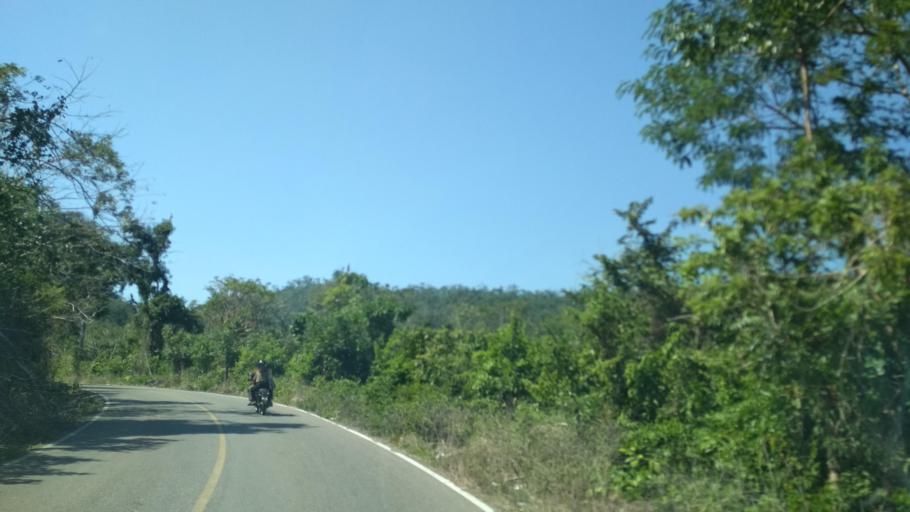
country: MX
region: Veracruz
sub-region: Papantla
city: Polutla
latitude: 20.4681
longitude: -97.2235
